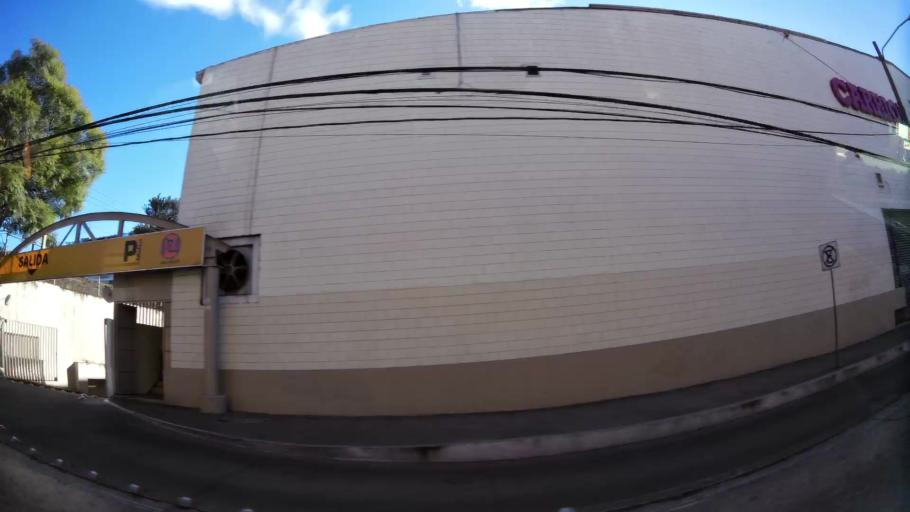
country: GT
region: Guatemala
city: Guatemala City
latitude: 14.6250
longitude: -90.5162
